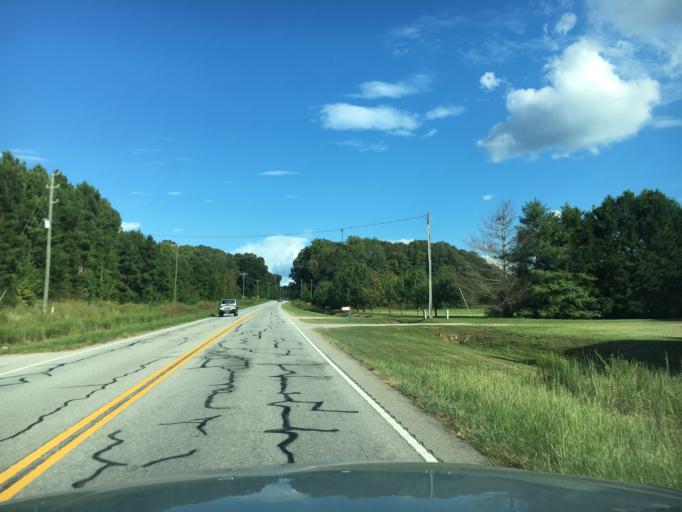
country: US
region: South Carolina
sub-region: Laurens County
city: Laurens
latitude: 34.5260
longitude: -82.1254
